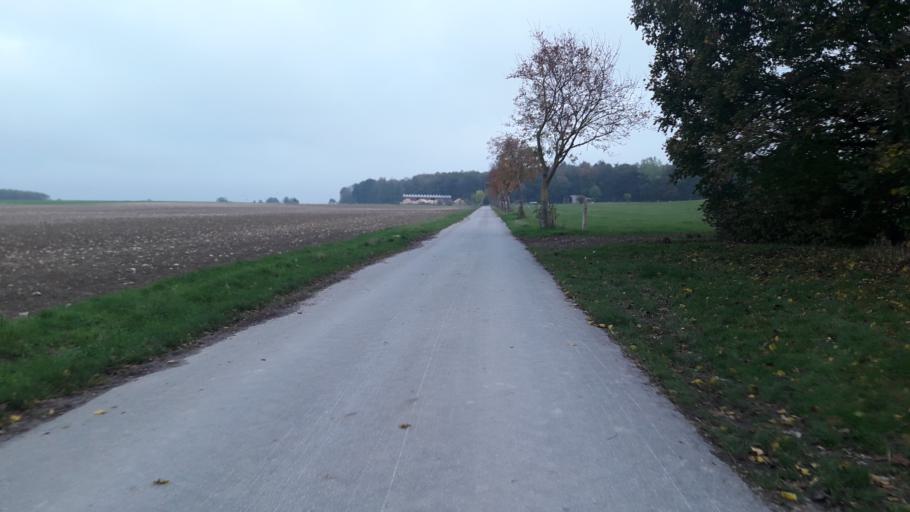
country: DE
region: North Rhine-Westphalia
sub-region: Regierungsbezirk Detmold
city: Paderborn
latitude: 51.6531
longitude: 8.7330
